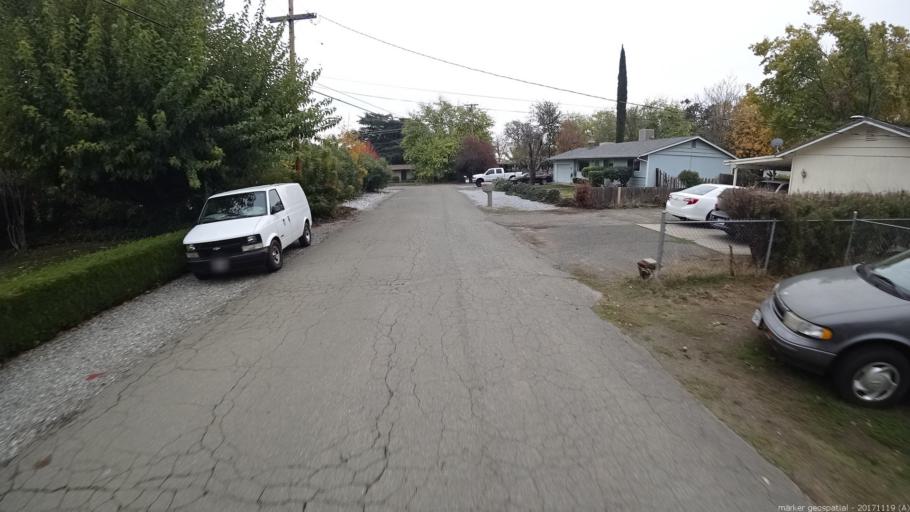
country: US
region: California
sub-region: Shasta County
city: Anderson
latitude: 40.4924
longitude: -122.3475
